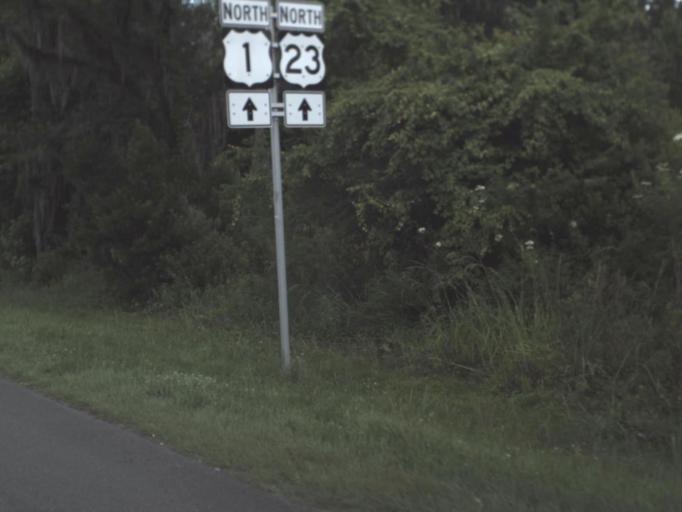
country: US
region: Florida
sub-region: Nassau County
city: Callahan
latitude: 30.5598
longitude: -81.8237
